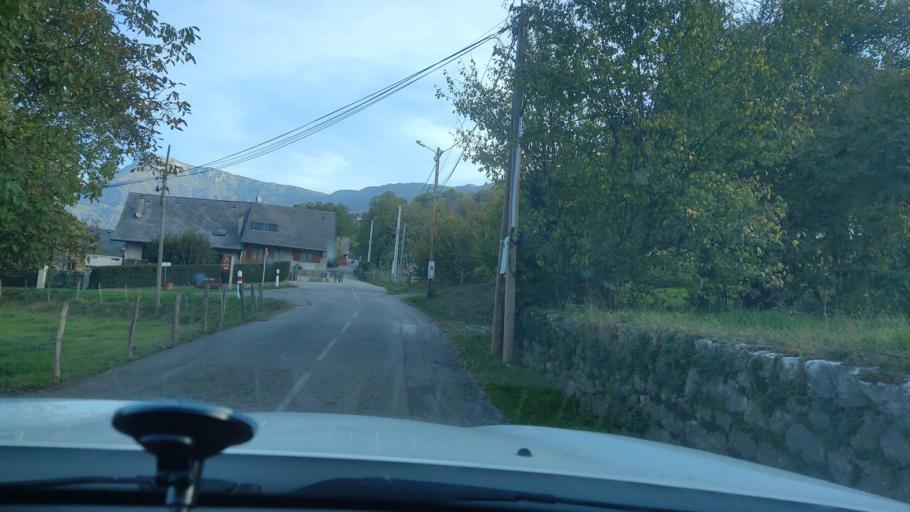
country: FR
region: Rhone-Alpes
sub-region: Departement de la Savoie
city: Barby
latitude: 45.5662
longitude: 6.0244
